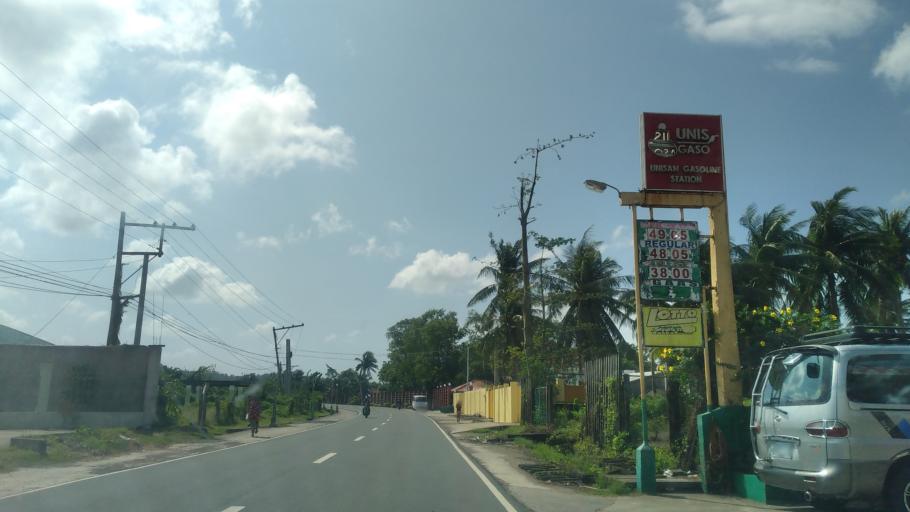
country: PH
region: Calabarzon
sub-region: Province of Quezon
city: Unisan
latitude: 13.8361
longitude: 121.9781
